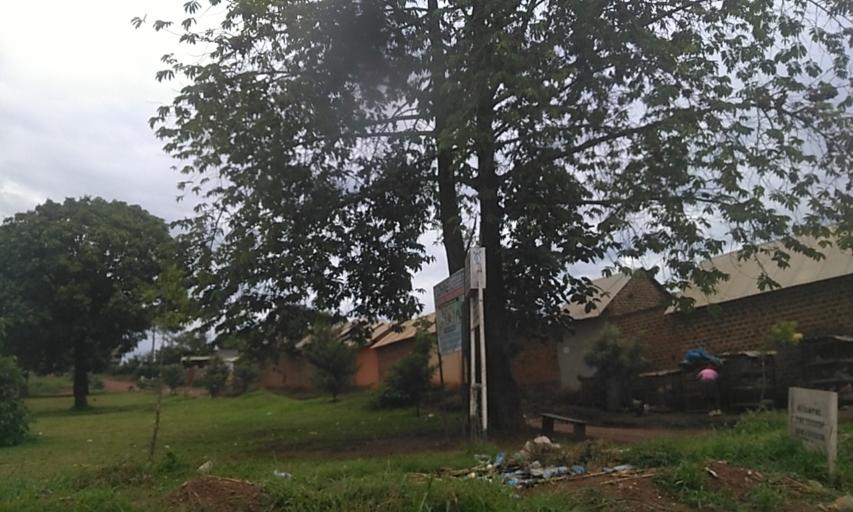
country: UG
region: Central Region
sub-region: Wakiso District
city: Bweyogerere
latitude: 0.3958
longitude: 32.6959
